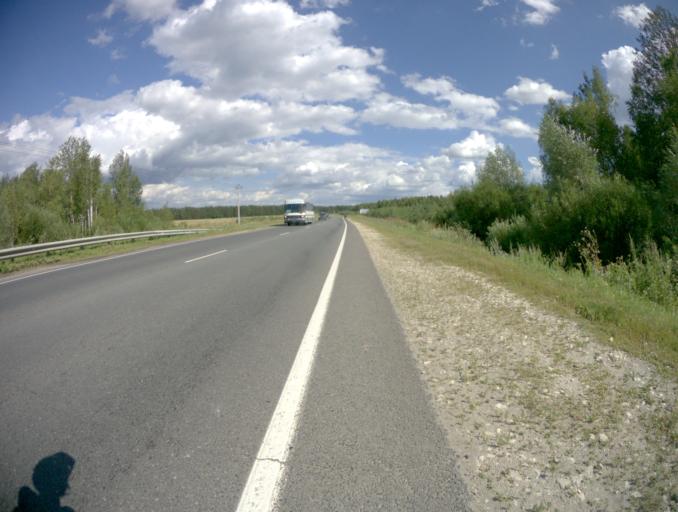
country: RU
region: Vladimir
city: Andreyevo
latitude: 55.9353
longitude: 41.0850
